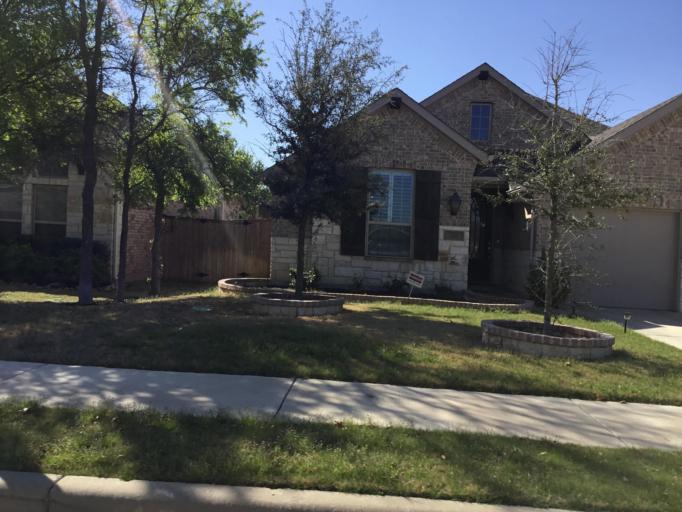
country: US
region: Texas
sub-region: Williamson County
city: Brushy Creek
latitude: 30.5729
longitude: -97.7683
